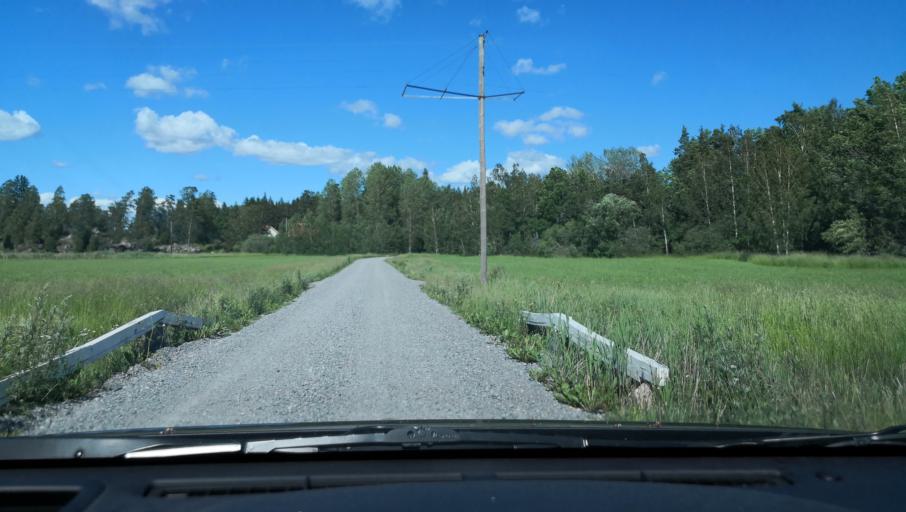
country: SE
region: Soedermanland
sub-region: Eskilstuna Kommun
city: Hallbybrunn
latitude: 59.3060
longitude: 16.3654
